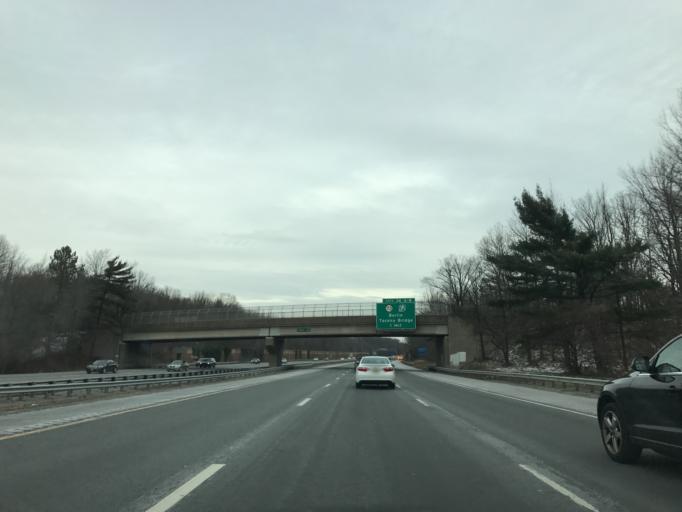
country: US
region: New Jersey
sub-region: Camden County
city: Kingston Estates
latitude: 39.9204
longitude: -74.9790
